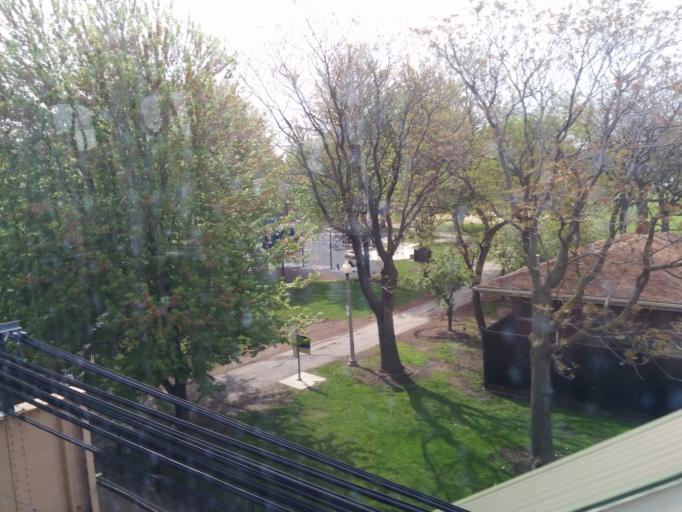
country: US
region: Illinois
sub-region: Cook County
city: Chicago
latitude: 41.8853
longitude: -87.6659
